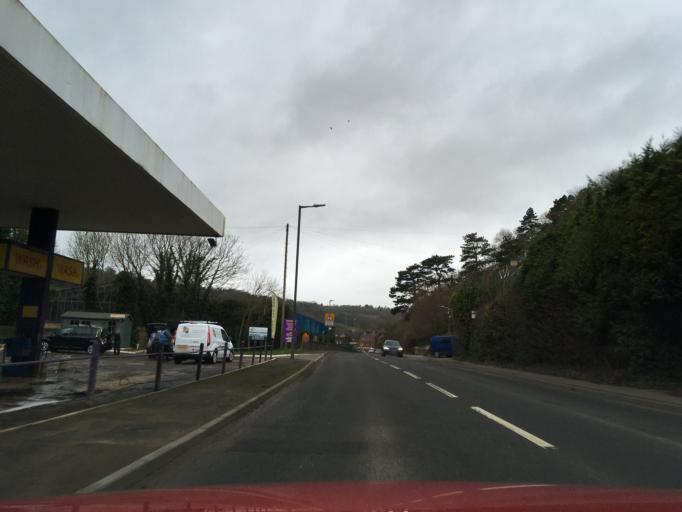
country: GB
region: England
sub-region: Gloucestershire
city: Brimscombe
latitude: 51.7189
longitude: -2.1873
